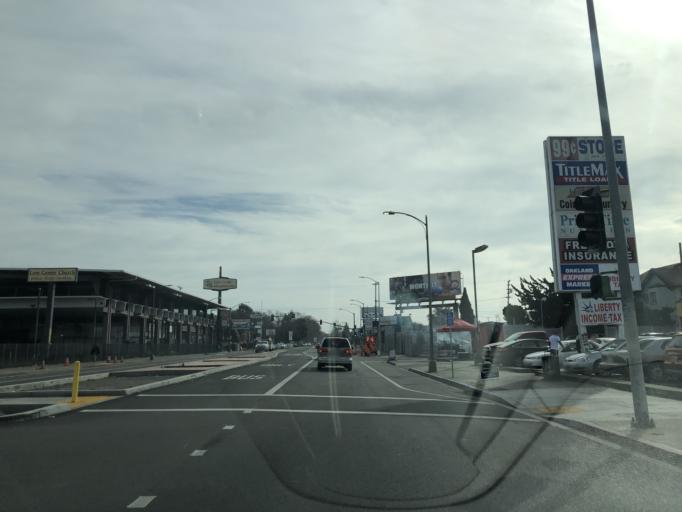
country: US
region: California
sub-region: Alameda County
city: San Leandro
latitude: 37.7403
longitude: -122.1676
